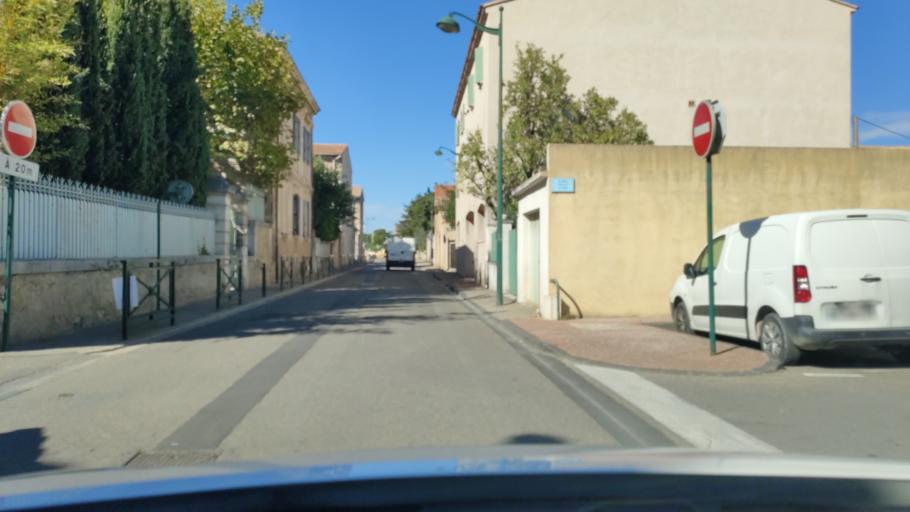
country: FR
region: Provence-Alpes-Cote d'Azur
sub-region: Departement du Vaucluse
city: Morieres-les-Avignon
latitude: 43.9425
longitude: 4.9047
